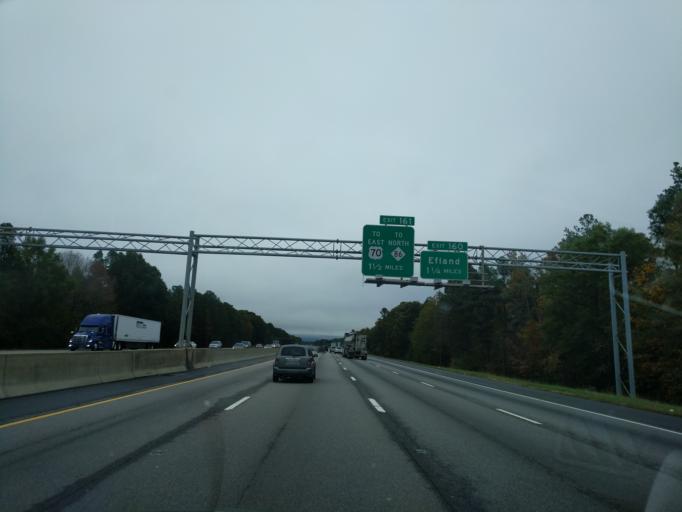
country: US
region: North Carolina
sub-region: Alamance County
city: Mebane
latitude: 36.0758
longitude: -79.1963
